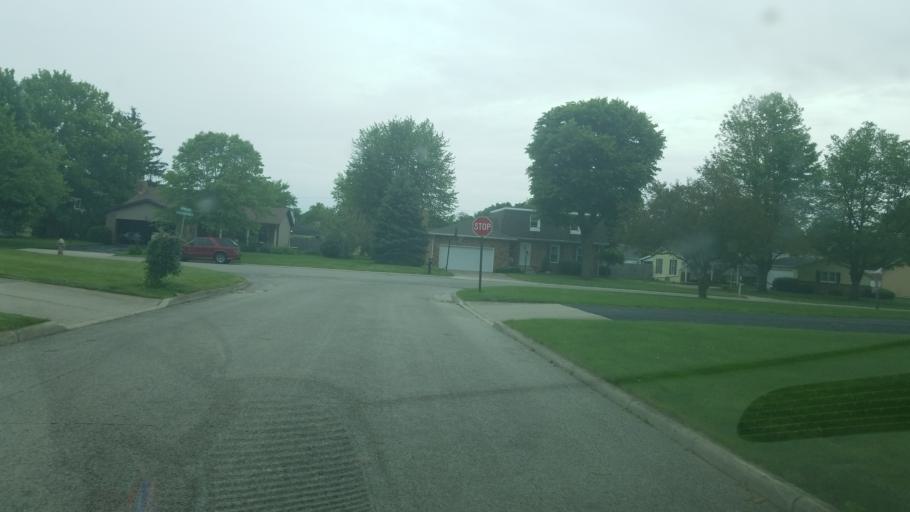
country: US
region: Ohio
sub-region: Crawford County
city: Bucyrus
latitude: 40.7961
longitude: -82.9893
